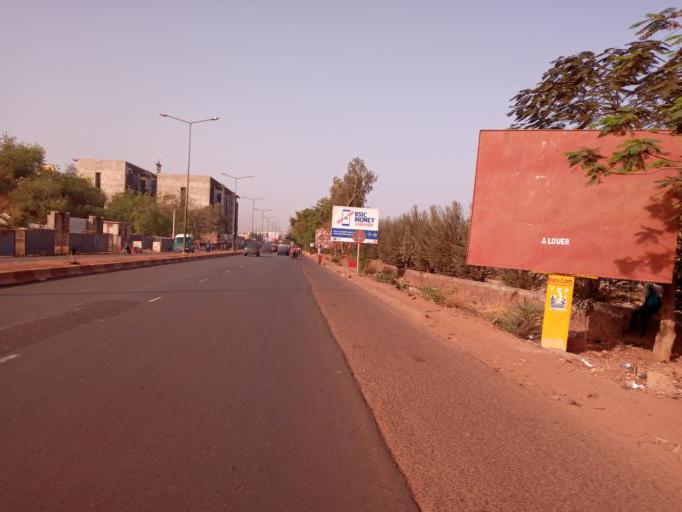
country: ML
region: Bamako
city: Bamako
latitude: 12.6153
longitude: -7.9902
